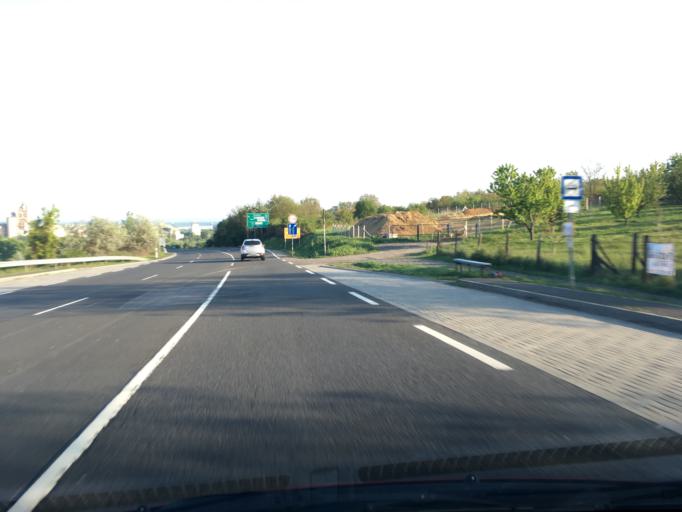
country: HU
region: Pest
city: Veroce
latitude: 47.8204
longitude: 19.0898
